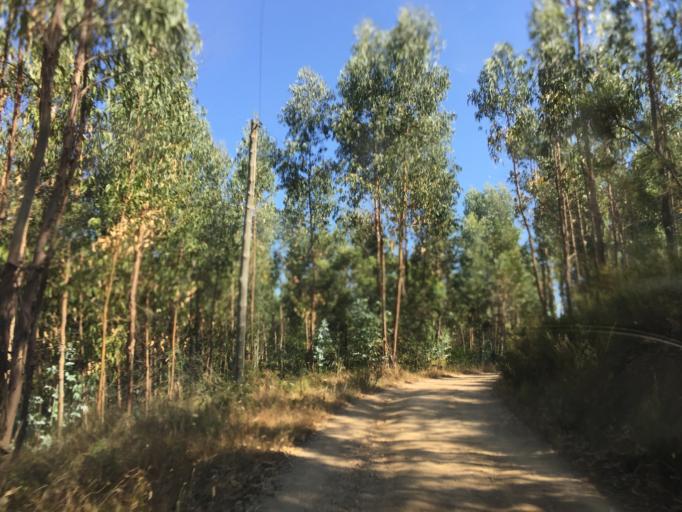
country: PT
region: Santarem
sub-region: Tomar
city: Tomar
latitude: 39.6093
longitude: -8.3492
